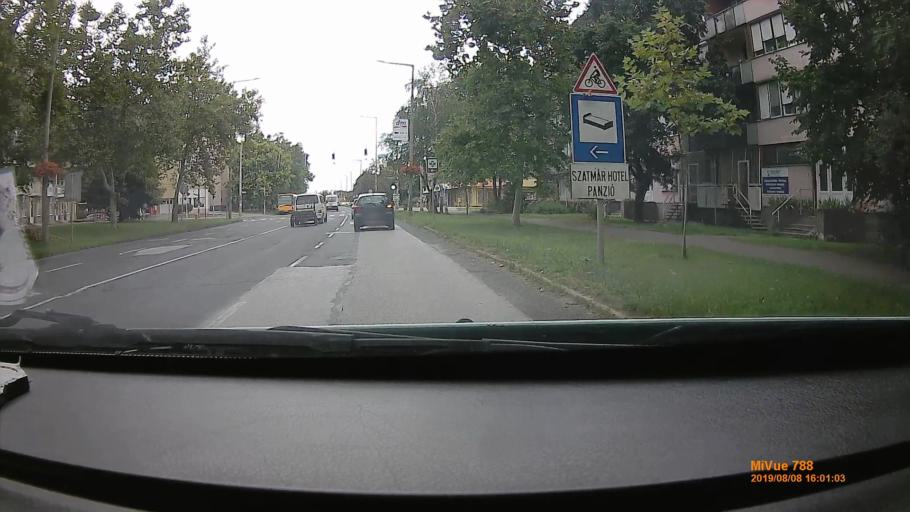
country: HU
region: Szabolcs-Szatmar-Bereg
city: Mateszalka
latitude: 47.9543
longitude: 22.3253
